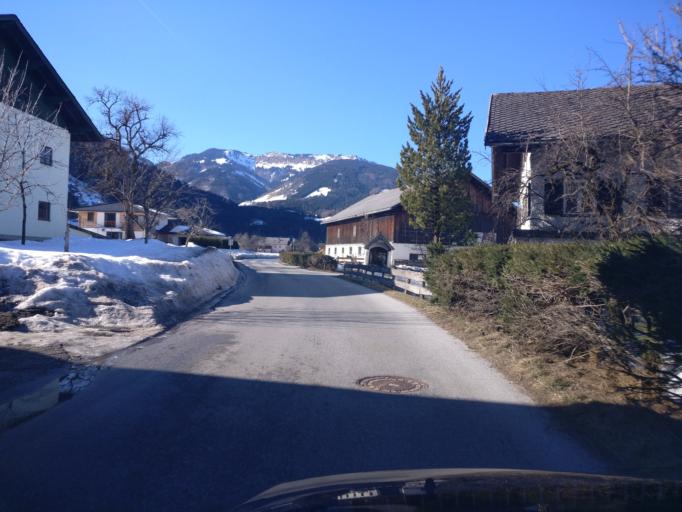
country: AT
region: Salzburg
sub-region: Politischer Bezirk Hallein
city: Golling an der Salzach
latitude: 47.5973
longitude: 13.1556
